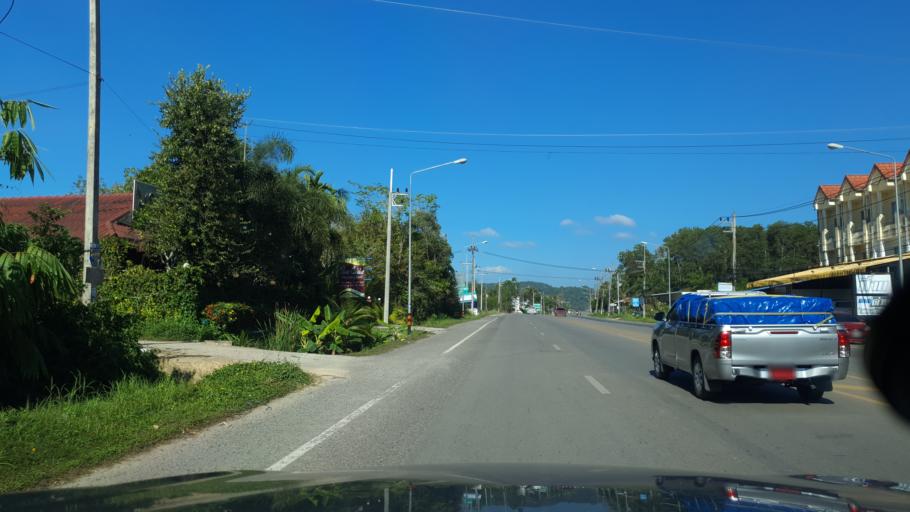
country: TH
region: Phangnga
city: Ban Ao Nang
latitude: 8.0341
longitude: 98.8592
